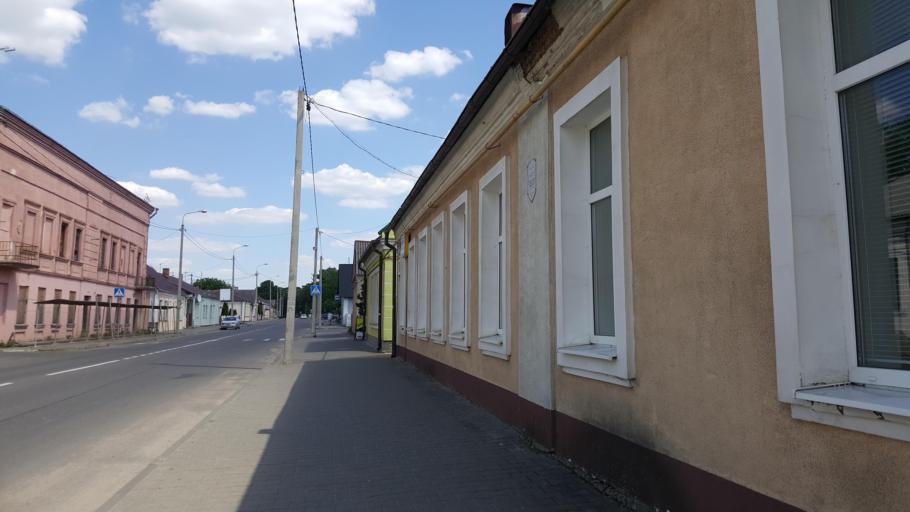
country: BY
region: Brest
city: Kobryn
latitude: 52.2124
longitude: 24.3611
